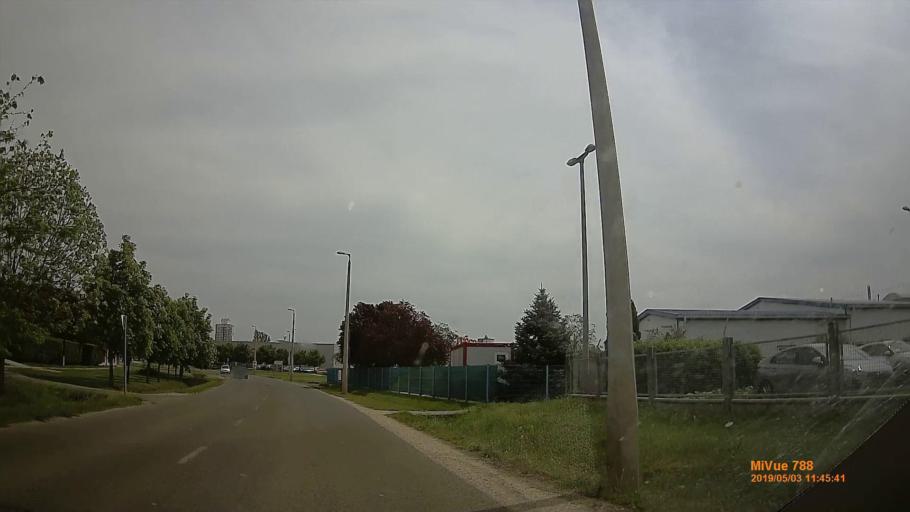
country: HU
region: Jasz-Nagykun-Szolnok
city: Szolnok
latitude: 47.1776
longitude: 20.1646
